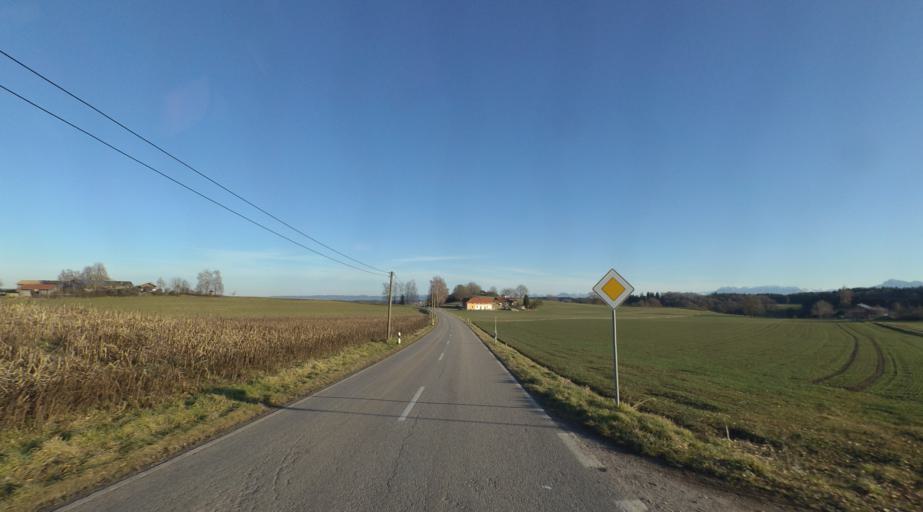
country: DE
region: Bavaria
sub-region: Upper Bavaria
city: Taching am See
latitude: 47.9953
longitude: 12.7127
